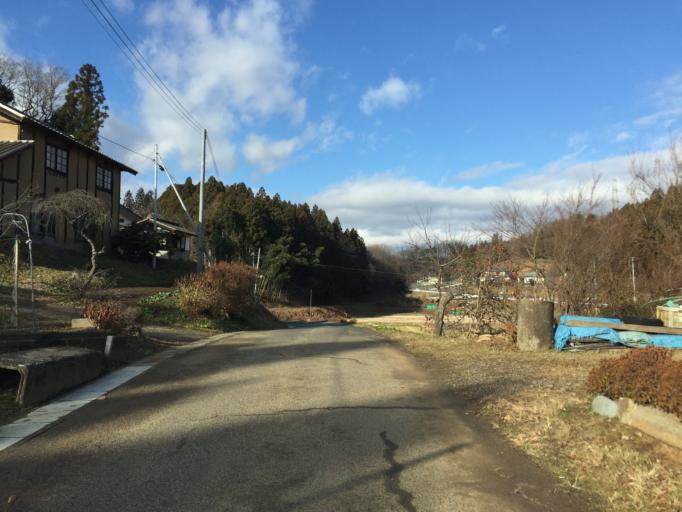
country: JP
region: Fukushima
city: Fukushima-shi
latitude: 37.6811
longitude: 140.4861
